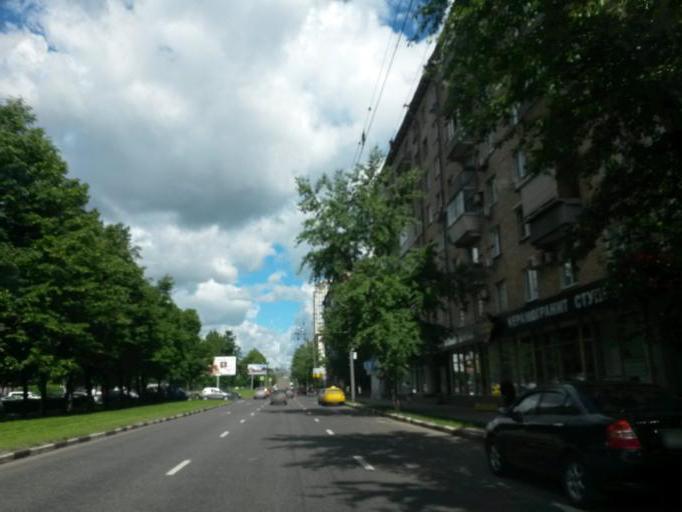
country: RU
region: Moskovskaya
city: Semenovskoye
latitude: 55.6804
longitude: 37.5592
